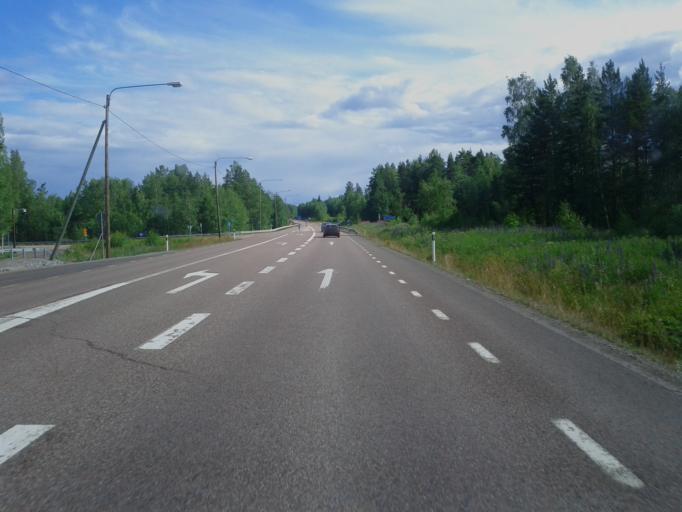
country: SE
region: Dalarna
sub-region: Faluns Kommun
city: Grycksbo
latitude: 60.6645
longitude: 15.5458
